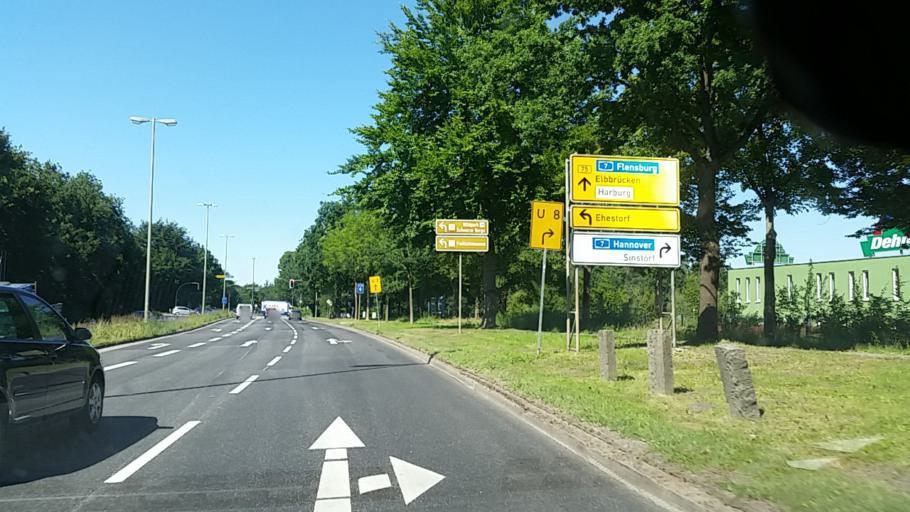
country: DE
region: Lower Saxony
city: Seevetal
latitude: 53.4298
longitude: 9.9320
